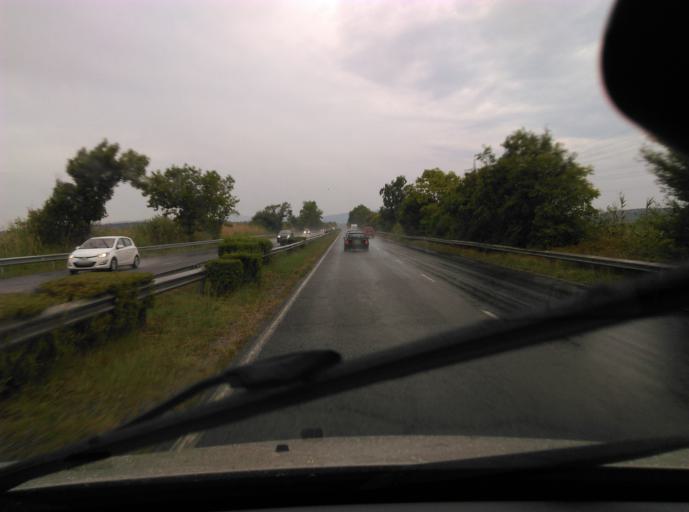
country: BG
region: Burgas
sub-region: Obshtina Burgas
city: Burgas
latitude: 42.4506
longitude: 27.4505
